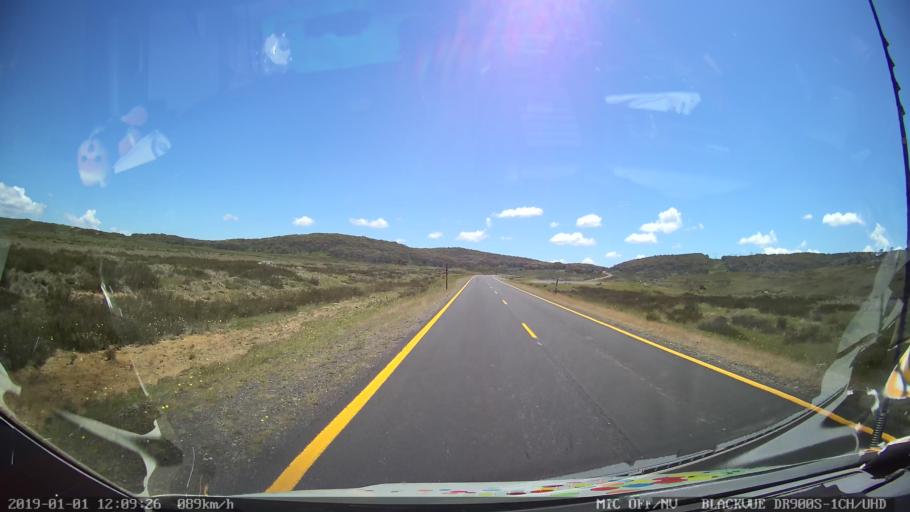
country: AU
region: New South Wales
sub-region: Tumut Shire
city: Tumut
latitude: -35.8073
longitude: 148.4960
